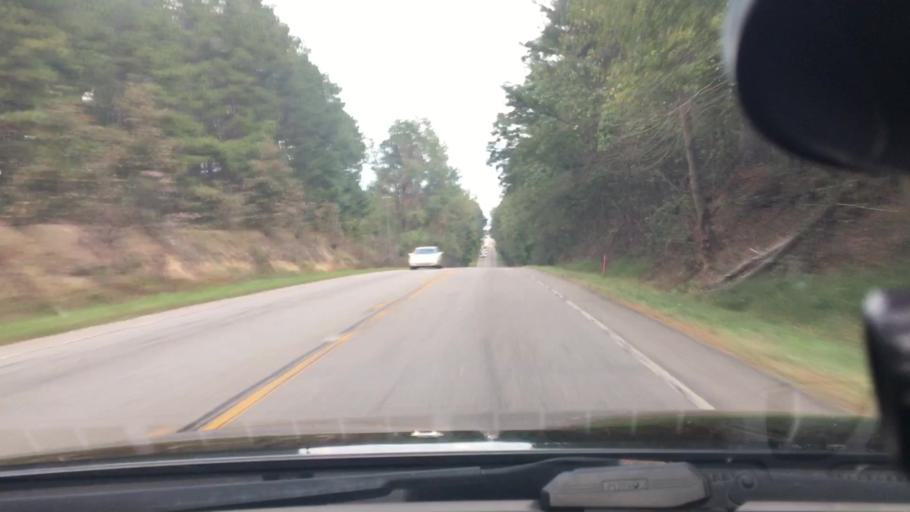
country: US
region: North Carolina
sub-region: Moore County
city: Carthage
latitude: 35.3481
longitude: -79.3730
